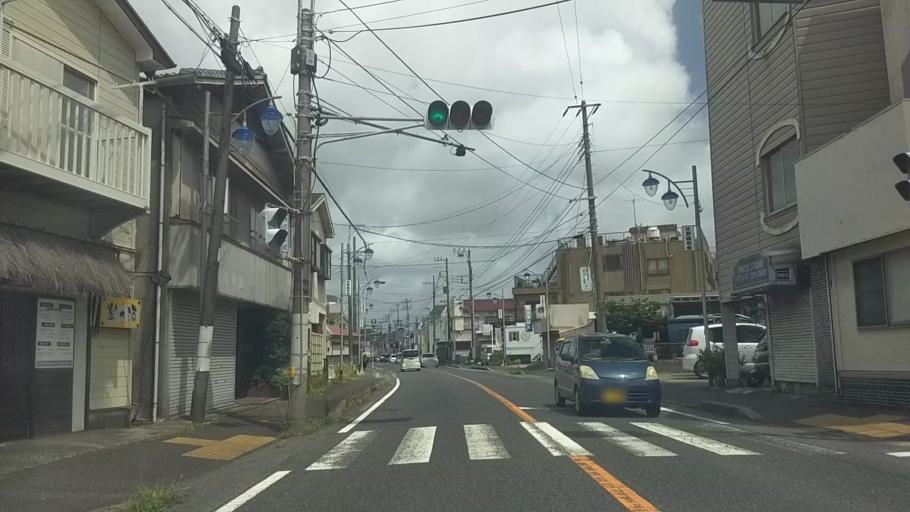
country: JP
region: Kanagawa
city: Yokosuka
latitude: 35.2600
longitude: 139.6686
